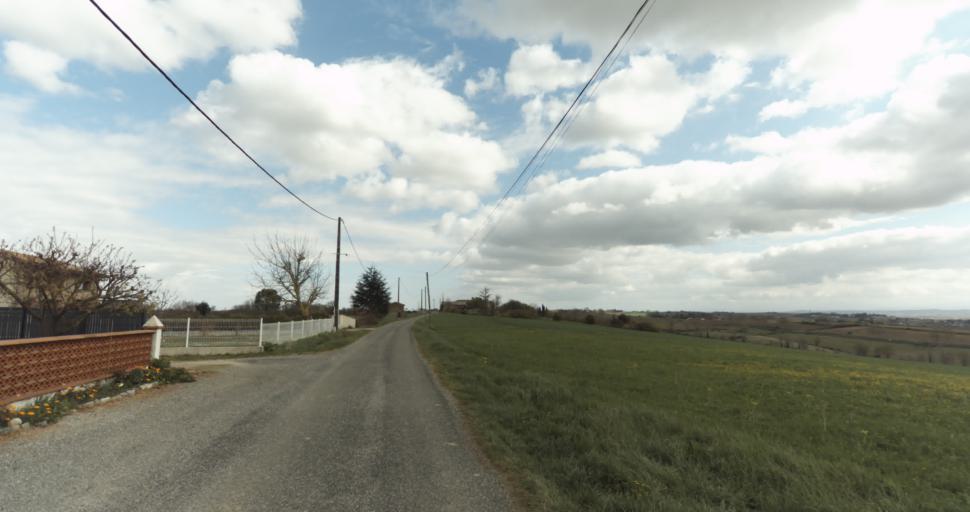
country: FR
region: Midi-Pyrenees
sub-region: Departement de la Haute-Garonne
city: Auterive
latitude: 43.3656
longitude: 1.4886
